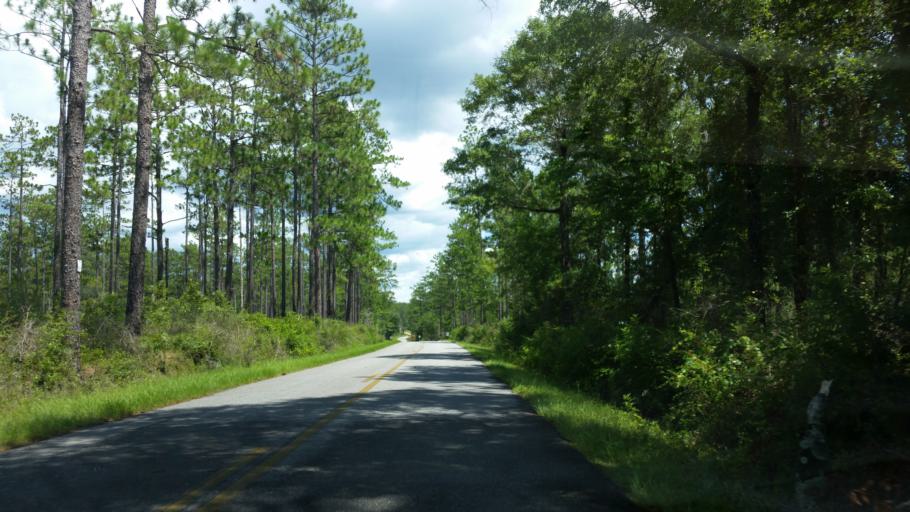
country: US
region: Florida
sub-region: Okaloosa County
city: Crestview
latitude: 30.7286
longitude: -86.8012
